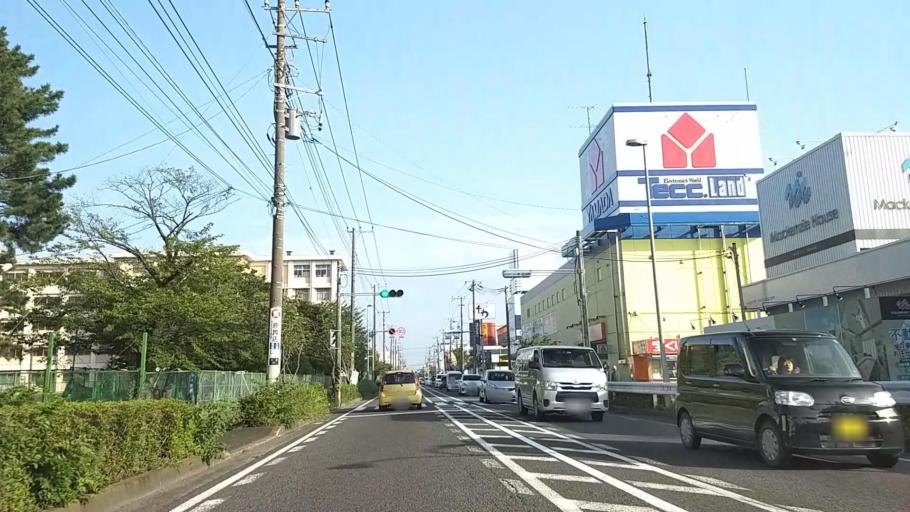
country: JP
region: Kanagawa
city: Hiratsuka
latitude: 35.3322
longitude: 139.3264
